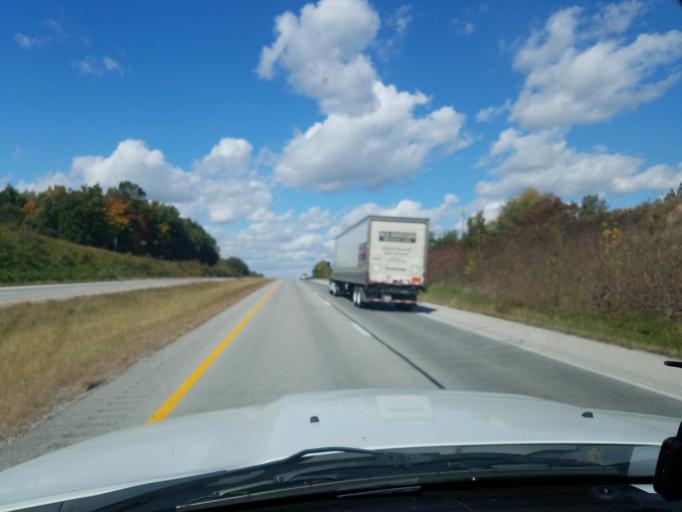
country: US
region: Kentucky
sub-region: Daviess County
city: Masonville
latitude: 37.6318
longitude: -86.9914
